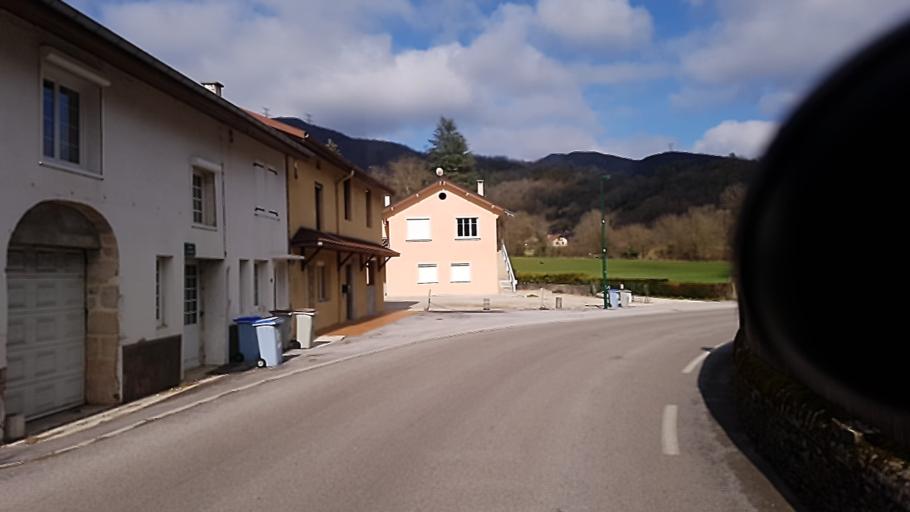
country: FR
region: Rhone-Alpes
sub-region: Departement de l'Ain
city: Izernore
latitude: 46.2697
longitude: 5.5269
